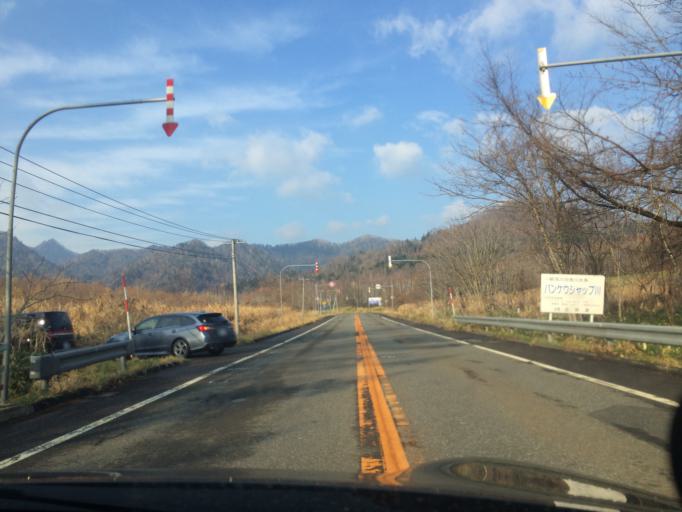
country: JP
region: Hokkaido
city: Shimo-furano
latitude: 42.8970
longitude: 142.4277
